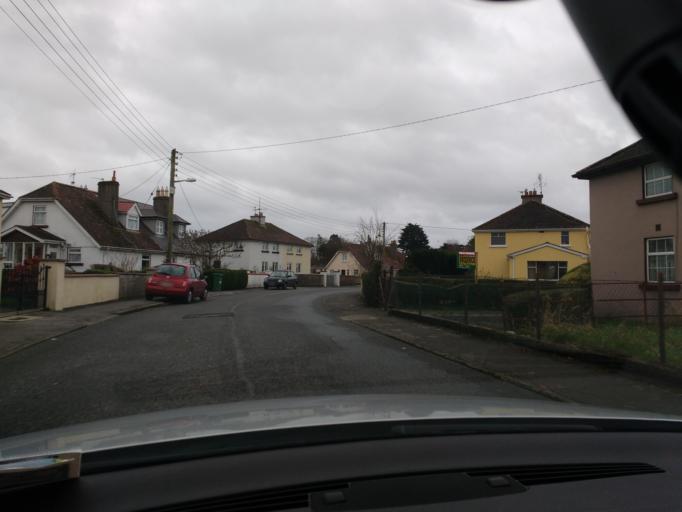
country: IE
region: Munster
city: Thurles
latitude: 52.6752
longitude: -7.8155
